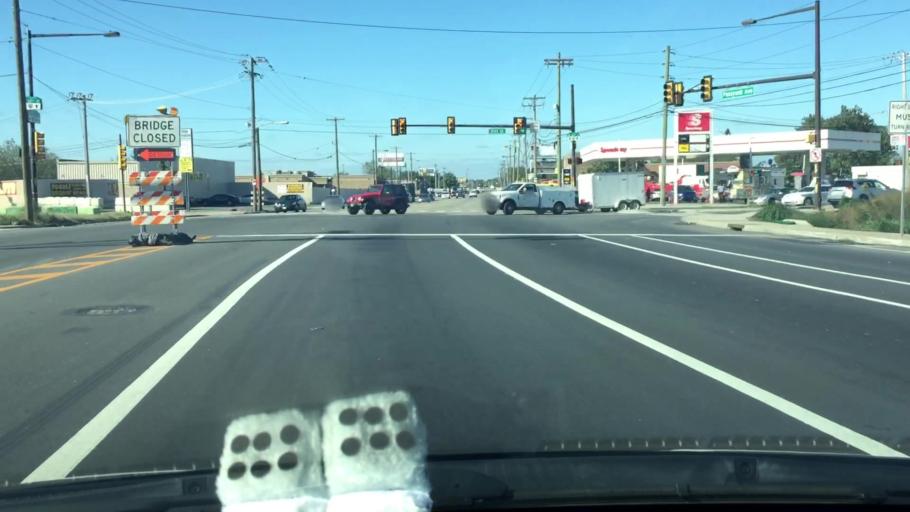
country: US
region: Pennsylvania
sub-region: Delaware County
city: Colwyn
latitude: 39.9184
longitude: -75.2085
